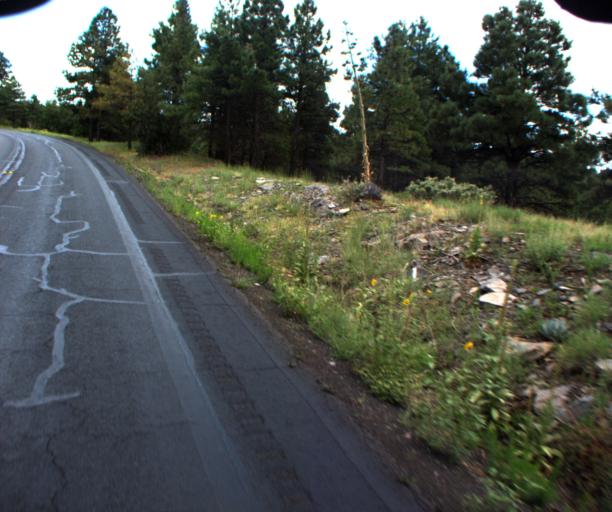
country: US
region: Arizona
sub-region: Gila County
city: Pine
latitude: 34.5141
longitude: -111.4883
